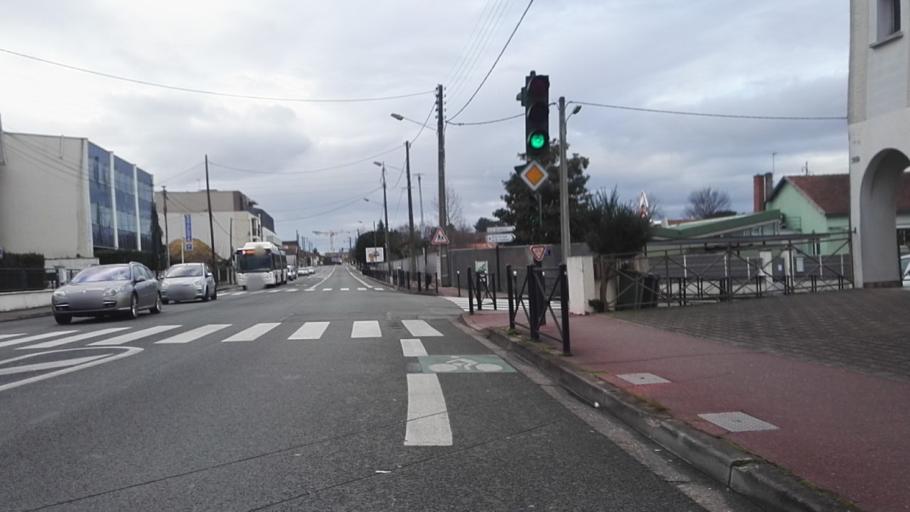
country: FR
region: Aquitaine
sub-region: Departement de la Gironde
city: Bruges
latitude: 44.8585
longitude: -0.6246
